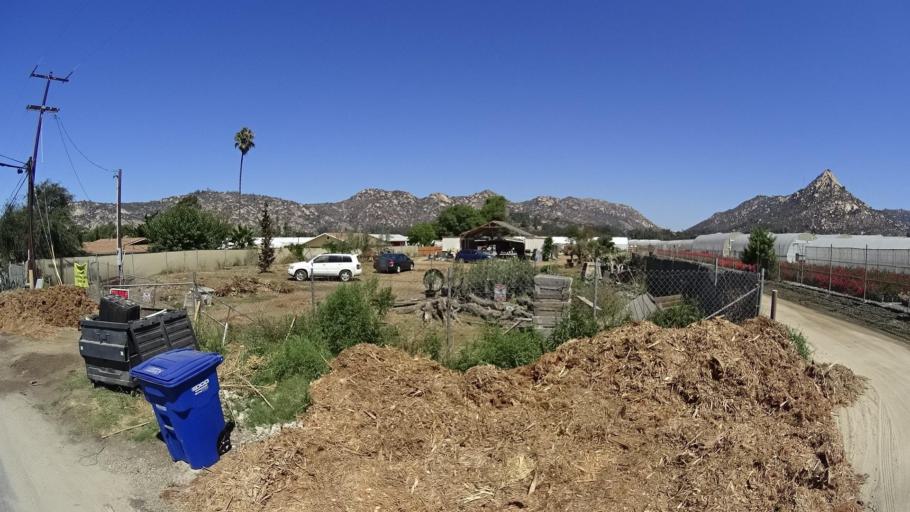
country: US
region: California
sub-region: San Diego County
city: Rainbow
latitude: 33.4139
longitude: -117.1433
